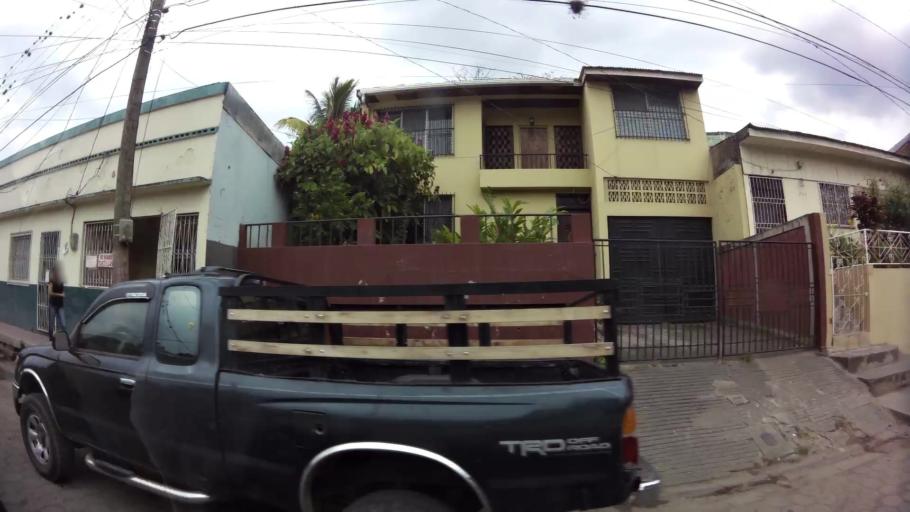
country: NI
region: Matagalpa
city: Matagalpa
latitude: 12.9317
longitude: -85.9190
